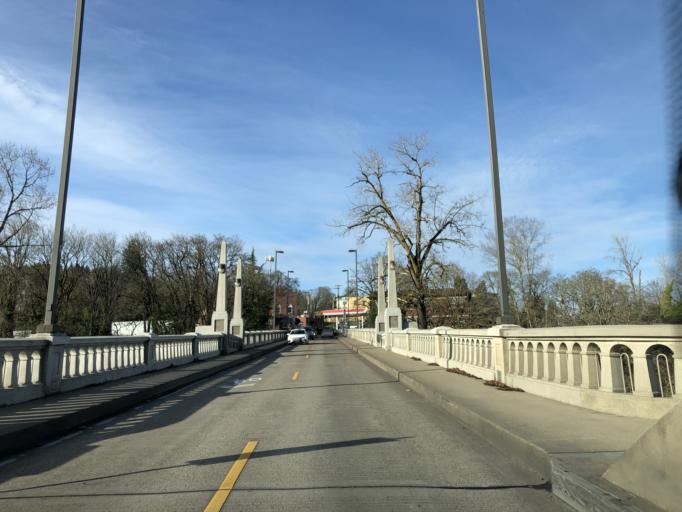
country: US
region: Oregon
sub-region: Clackamas County
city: Oregon City
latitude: 45.3589
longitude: -122.6097
